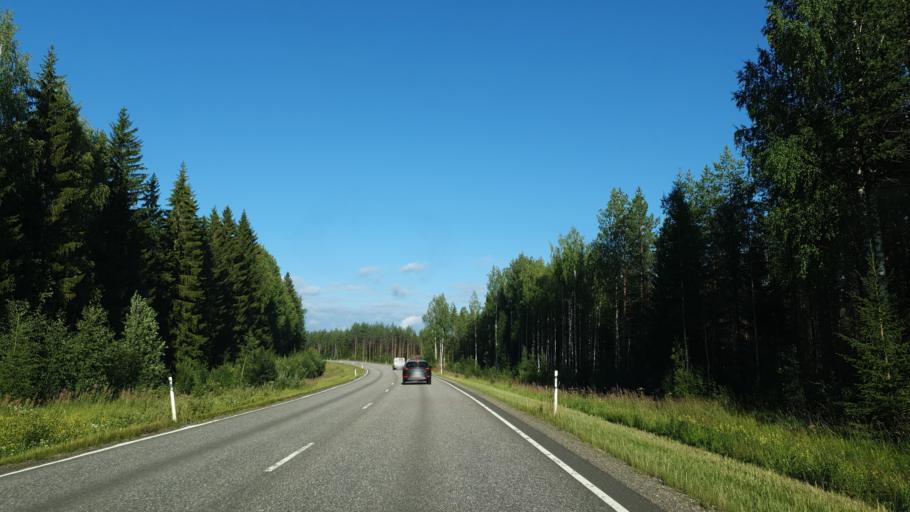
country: FI
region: North Karelia
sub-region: Joensuu
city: Outokumpu
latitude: 62.5198
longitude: 29.0162
